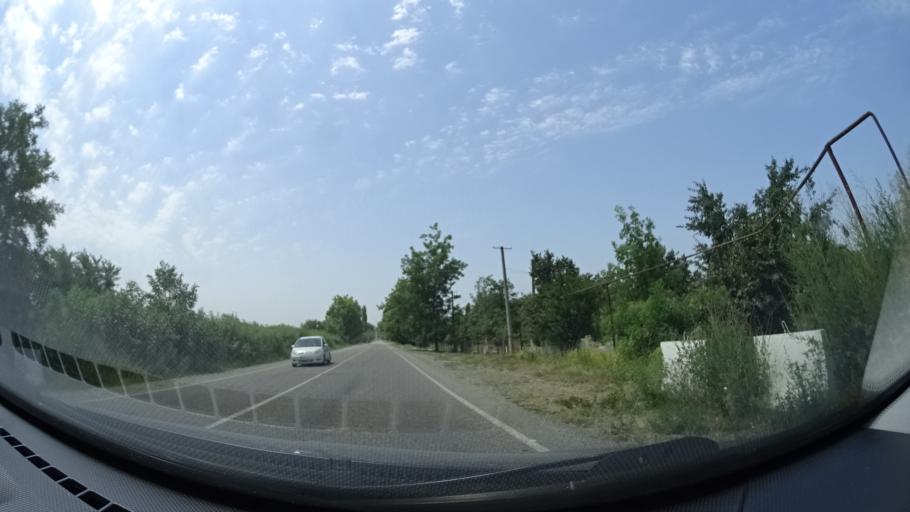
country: GE
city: Bagdadi
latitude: 41.7639
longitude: 46.1228
